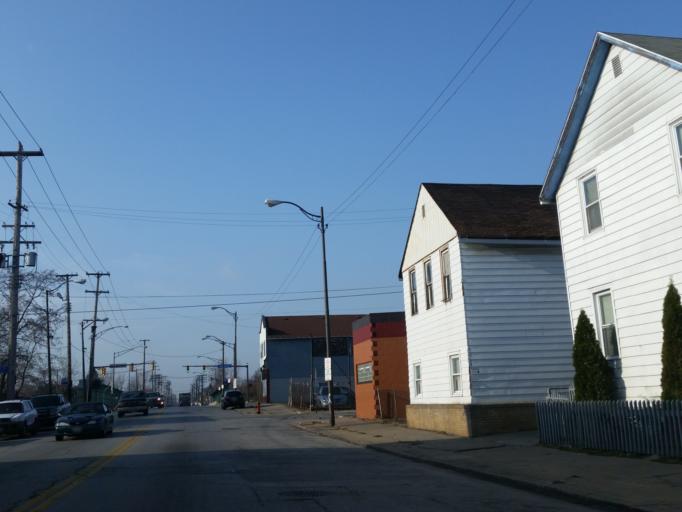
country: US
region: Ohio
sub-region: Cuyahoga County
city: Cleveland
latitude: 41.4766
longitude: -81.7242
